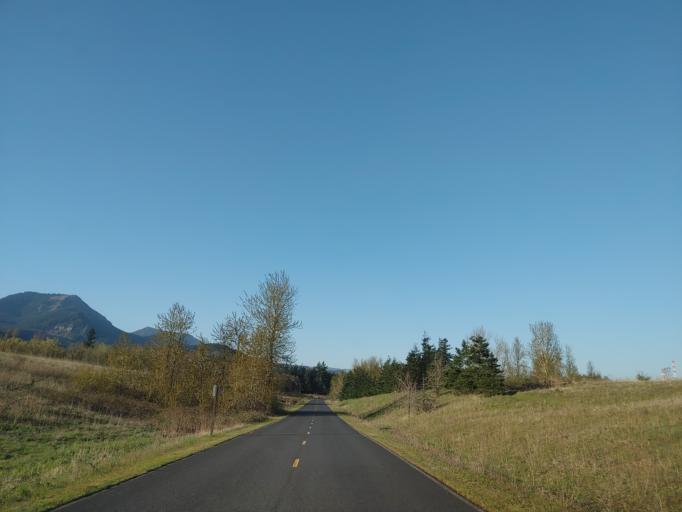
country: US
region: Oregon
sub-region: Hood River County
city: Cascade Locks
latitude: 45.6335
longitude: -121.9699
